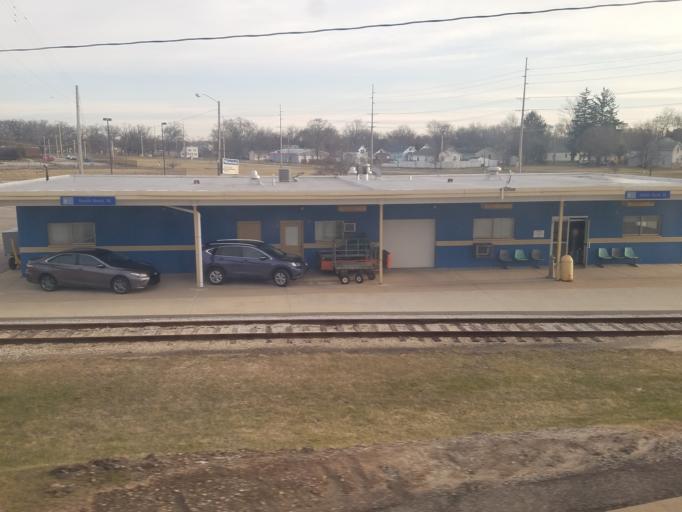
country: US
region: Indiana
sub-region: Saint Joseph County
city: South Bend
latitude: 41.6780
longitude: -86.2876
